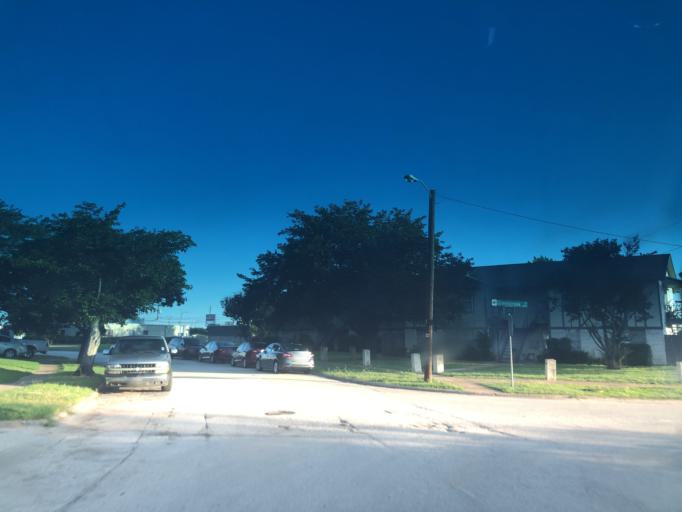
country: US
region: Texas
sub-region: Dallas County
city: Grand Prairie
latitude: 32.7078
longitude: -97.0140
